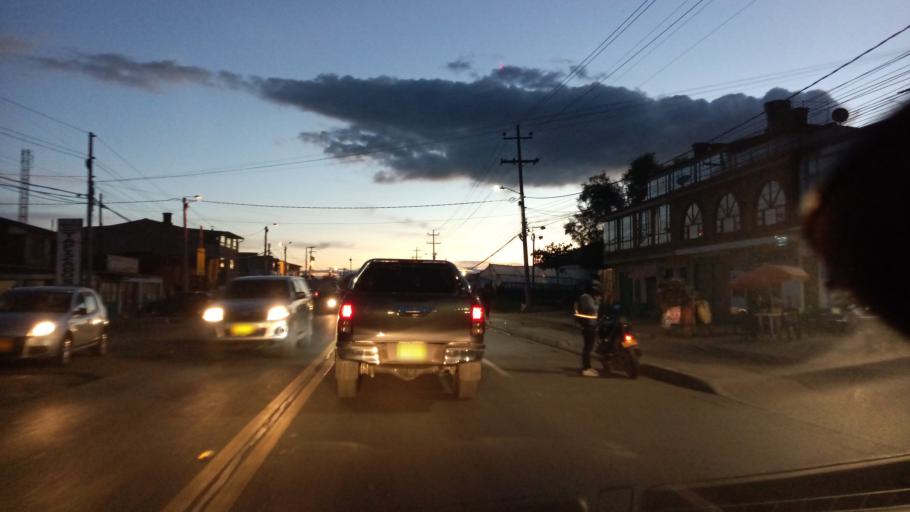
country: CO
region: Cundinamarca
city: Cota
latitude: 4.8176
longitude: -74.0954
